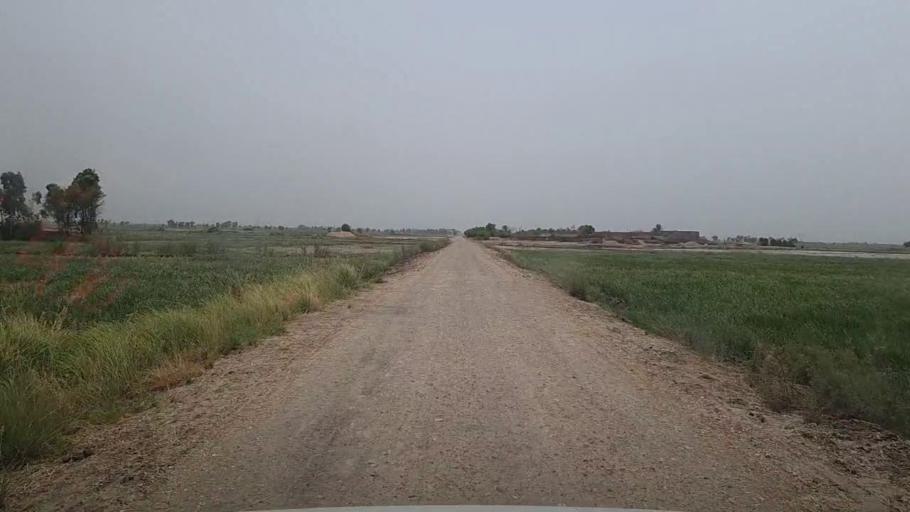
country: PK
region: Sindh
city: Sita Road
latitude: 27.0649
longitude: 67.8600
